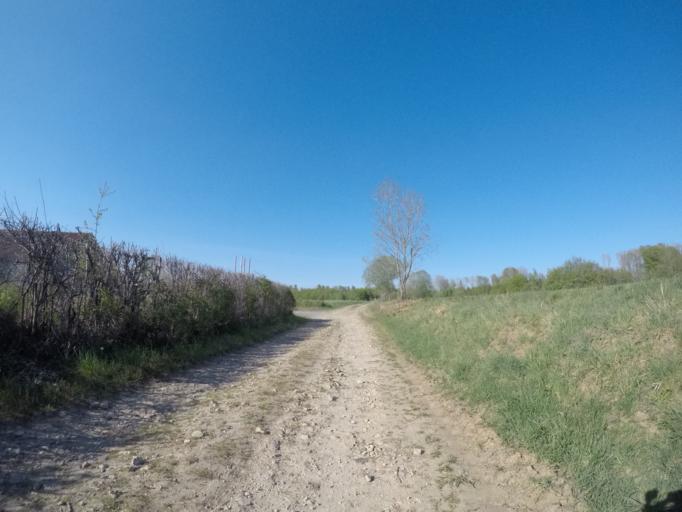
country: BE
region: Wallonia
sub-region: Province du Luxembourg
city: Tintigny
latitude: 49.7185
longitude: 5.5256
